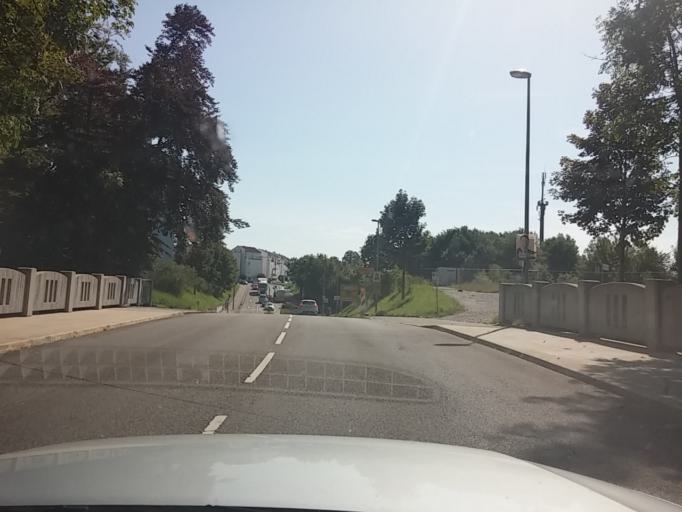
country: DE
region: Baden-Wuerttemberg
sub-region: Tuebingen Region
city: Leutkirch im Allgau
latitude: 47.8297
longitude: 10.0190
